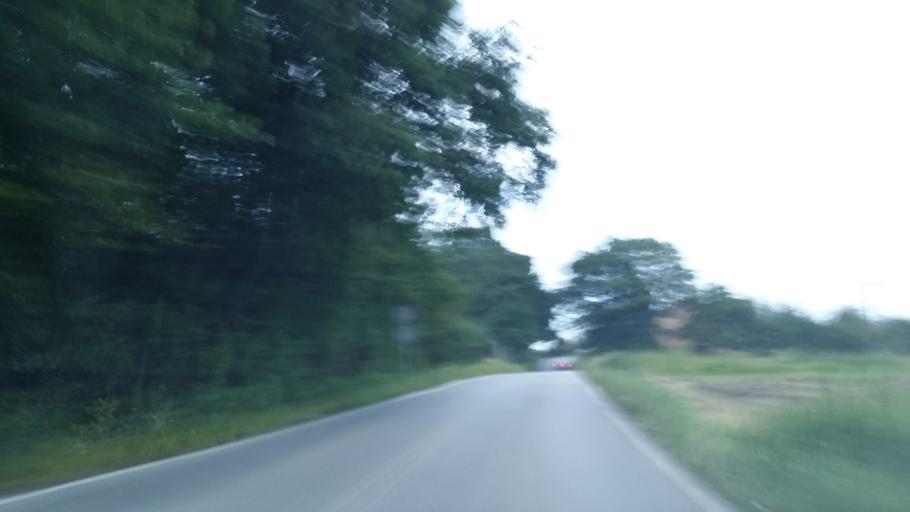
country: PL
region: Lesser Poland Voivodeship
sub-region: Powiat krakowski
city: Wolowice
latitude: 50.0121
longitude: 19.7127
